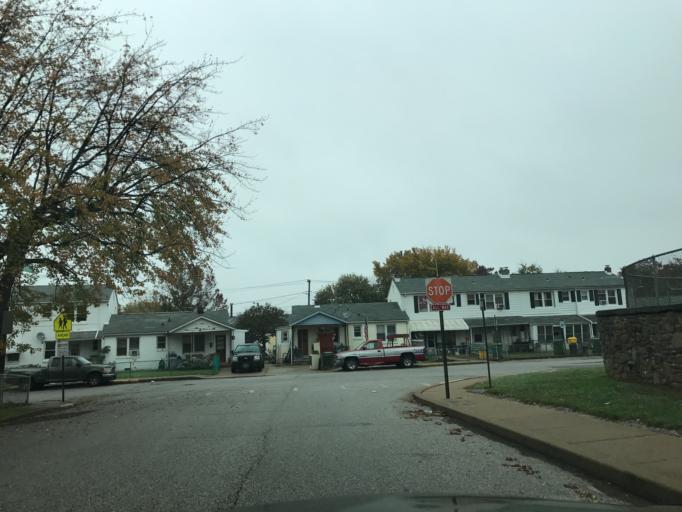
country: US
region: Maryland
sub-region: Baltimore County
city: Rosedale
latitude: 39.3052
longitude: -76.5524
